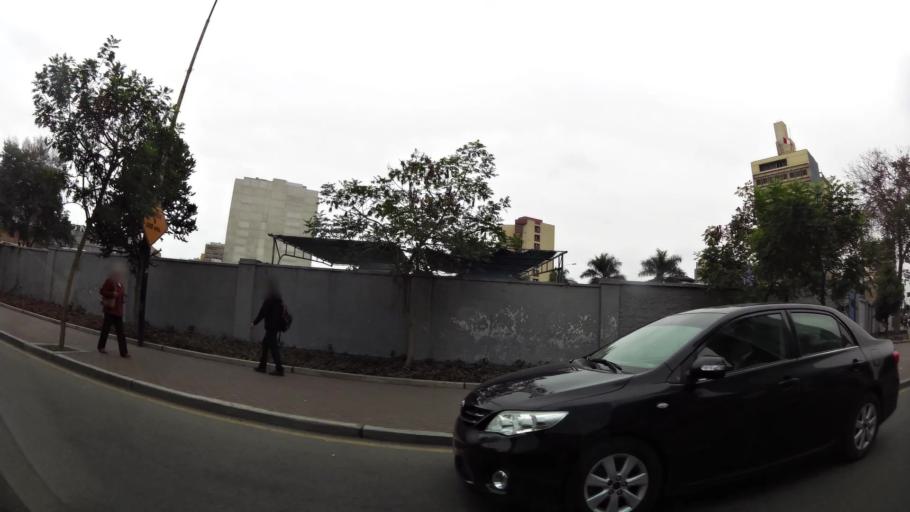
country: PE
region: Lima
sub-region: Lima
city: San Isidro
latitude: -12.0929
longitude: -77.0345
